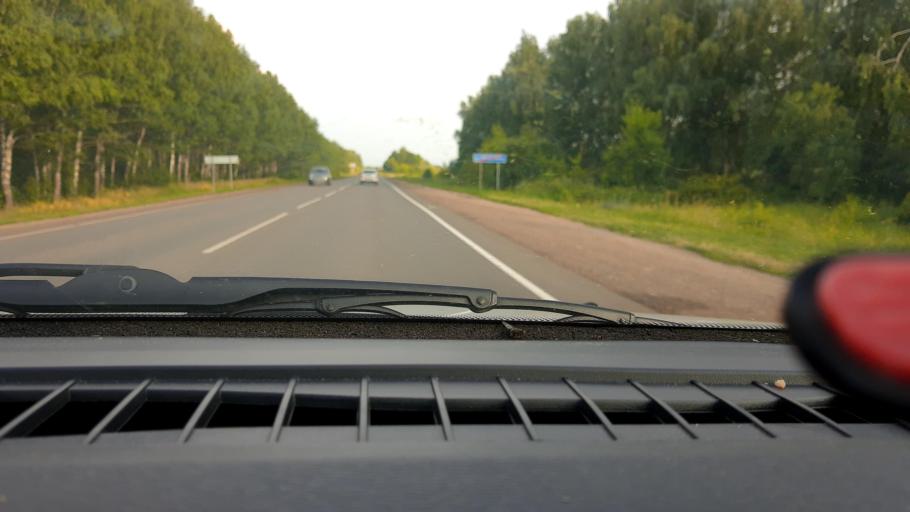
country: RU
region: Nizjnij Novgorod
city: Arzamas
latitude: 55.2937
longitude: 43.9397
